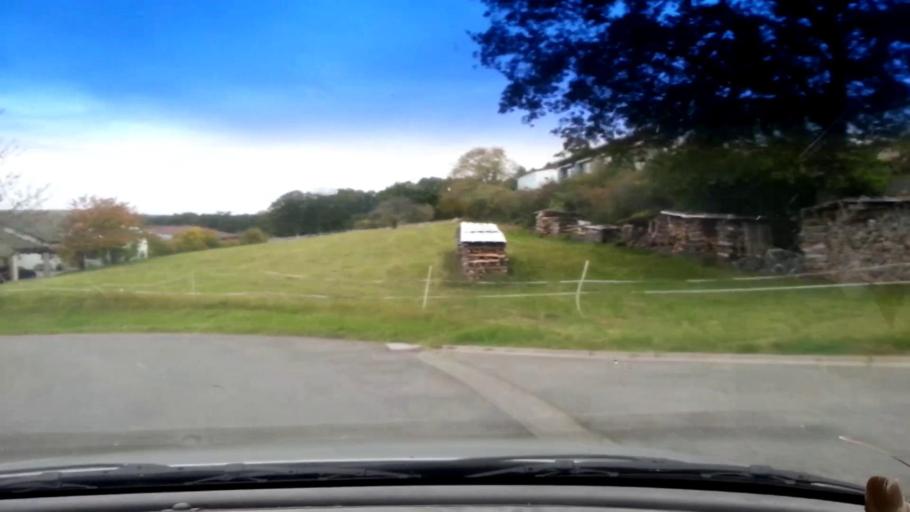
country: DE
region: Bavaria
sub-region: Upper Franconia
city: Priesendorf
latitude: 49.9104
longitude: 10.7049
